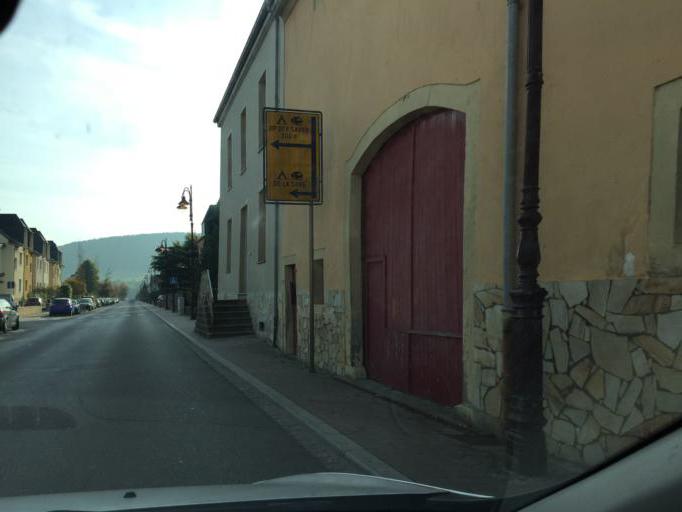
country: LU
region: Diekirch
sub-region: Canton de Diekirch
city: Diekirch
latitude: 49.8660
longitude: 6.1643
